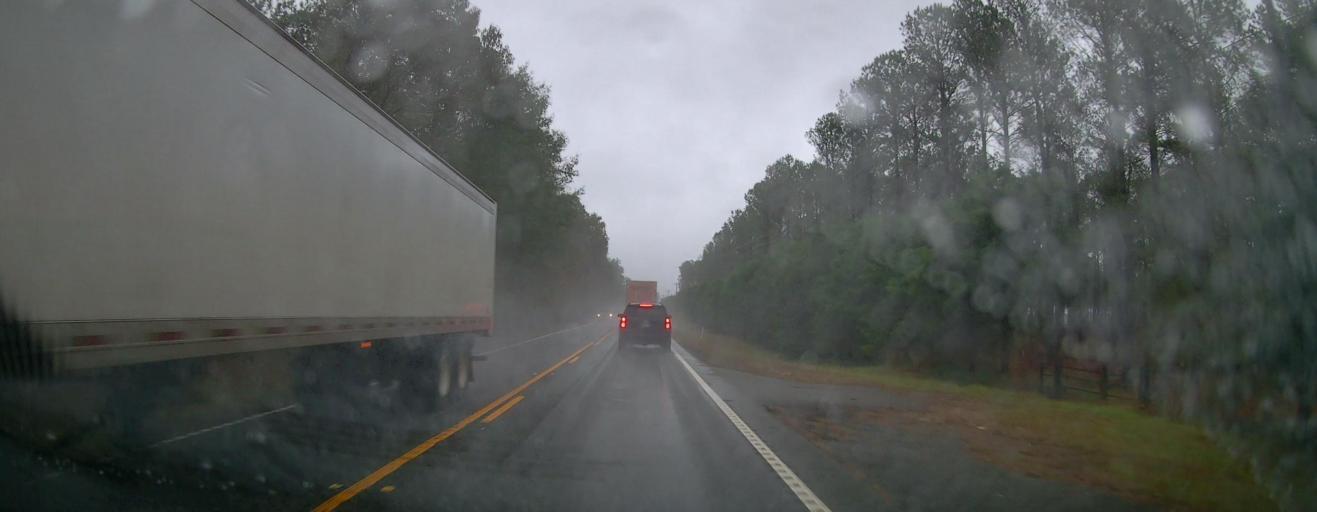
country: US
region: Georgia
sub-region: Jones County
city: Gray
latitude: 33.1302
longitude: -83.4723
